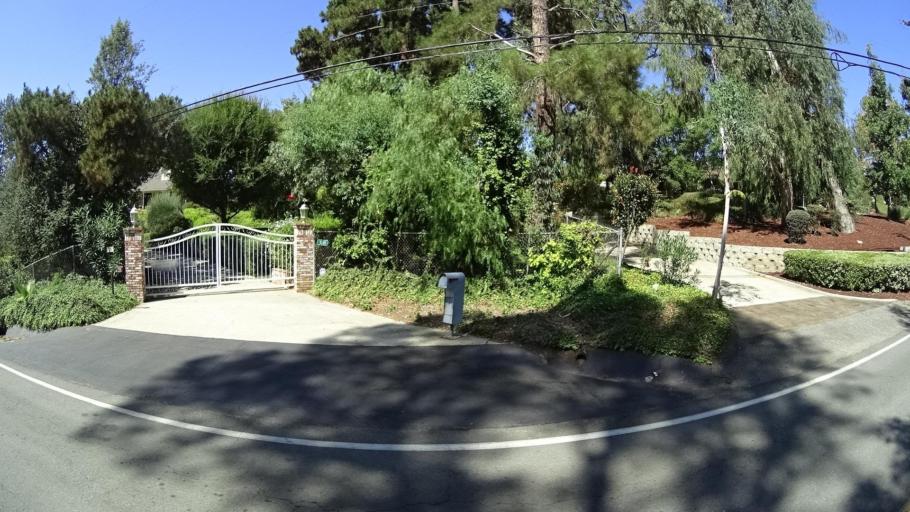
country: US
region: California
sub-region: San Diego County
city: Fallbrook
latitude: 33.3515
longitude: -117.2154
